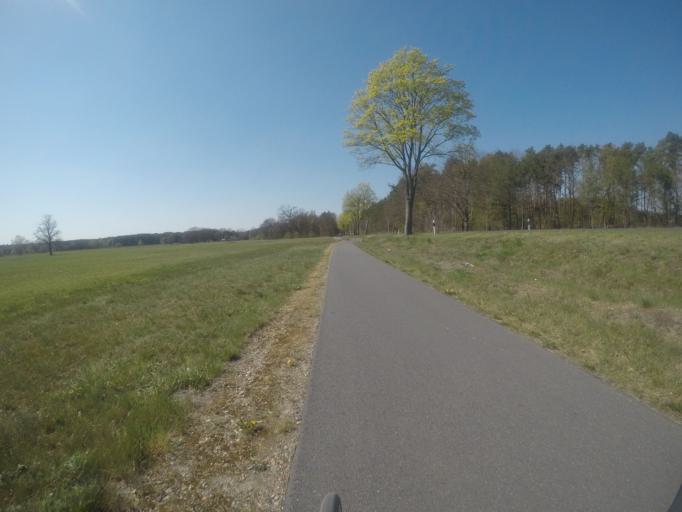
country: DE
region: Brandenburg
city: Birkenwerder
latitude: 52.7597
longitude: 13.3406
